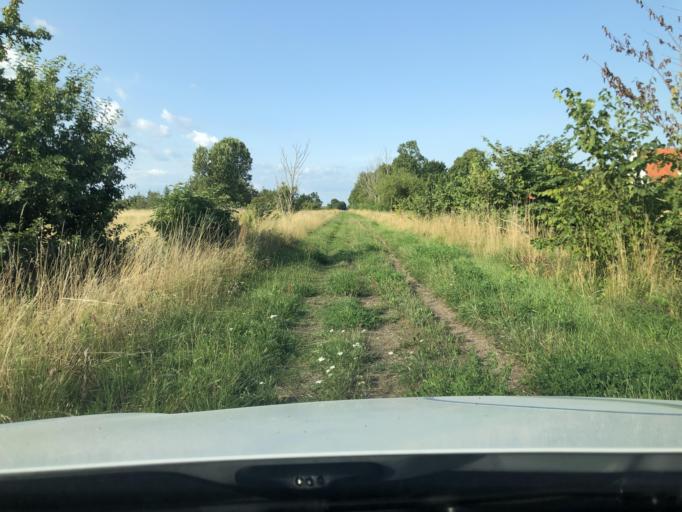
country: SE
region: Skane
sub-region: Kristianstads Kommun
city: Norra Asum
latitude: 55.9458
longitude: 14.1486
